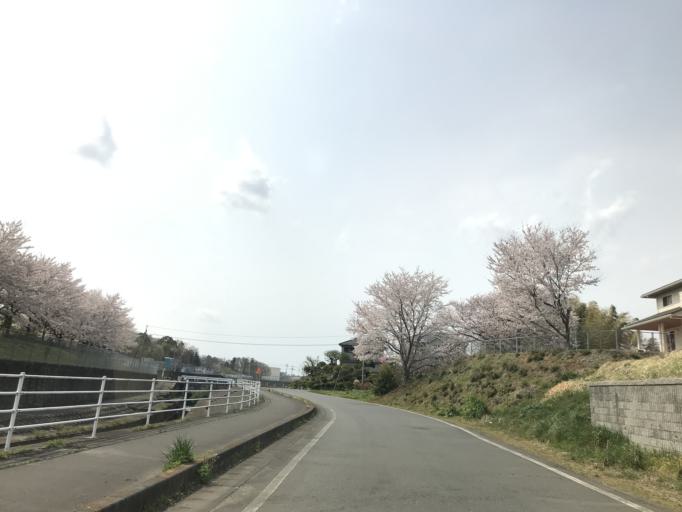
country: JP
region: Ibaraki
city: Moriya
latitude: 35.9650
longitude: 139.9936
